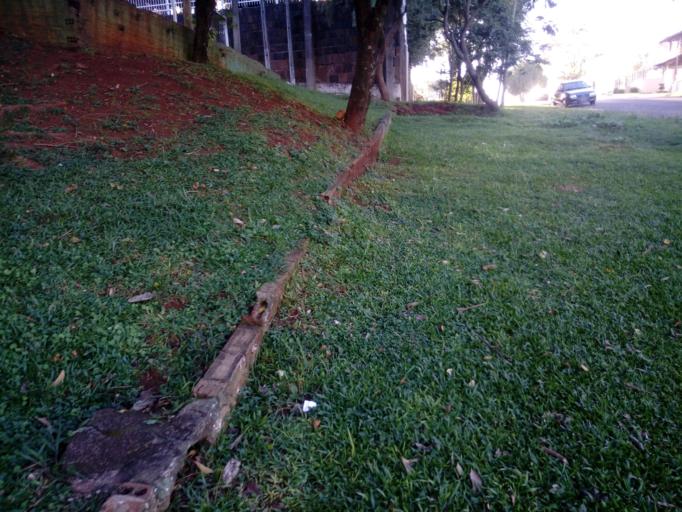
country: BR
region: Santa Catarina
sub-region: Chapeco
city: Chapeco
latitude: -27.1157
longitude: -52.6129
